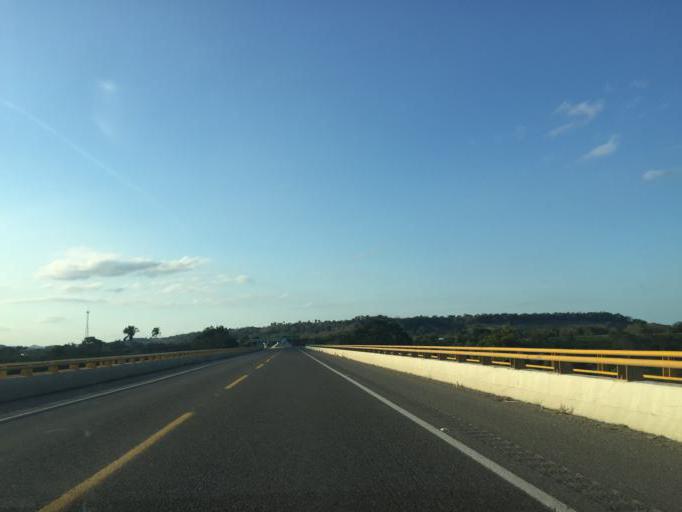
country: MX
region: Veracruz
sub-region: Papantla
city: Residencial Tajin
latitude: 20.6370
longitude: -97.4003
